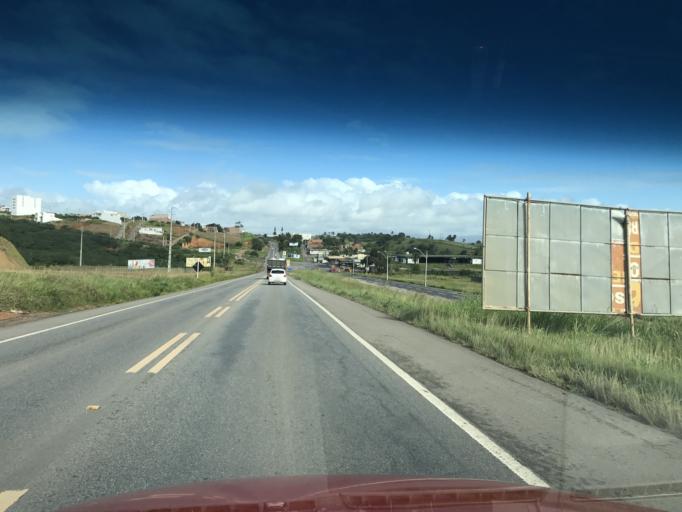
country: BR
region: Bahia
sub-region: Santo Antonio De Jesus
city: Santo Antonio de Jesus
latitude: -12.9557
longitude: -39.2608
